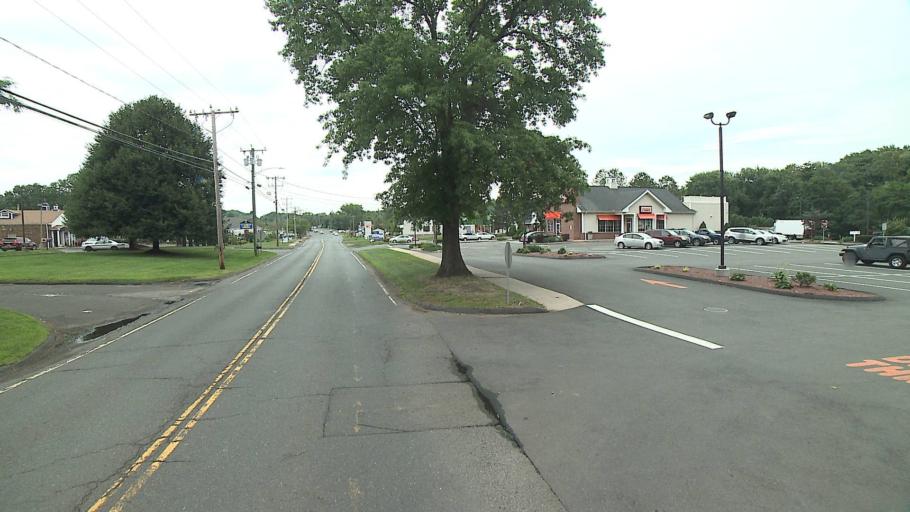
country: US
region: Connecticut
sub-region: Middlesex County
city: Cromwell
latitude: 41.5997
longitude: -72.6768
